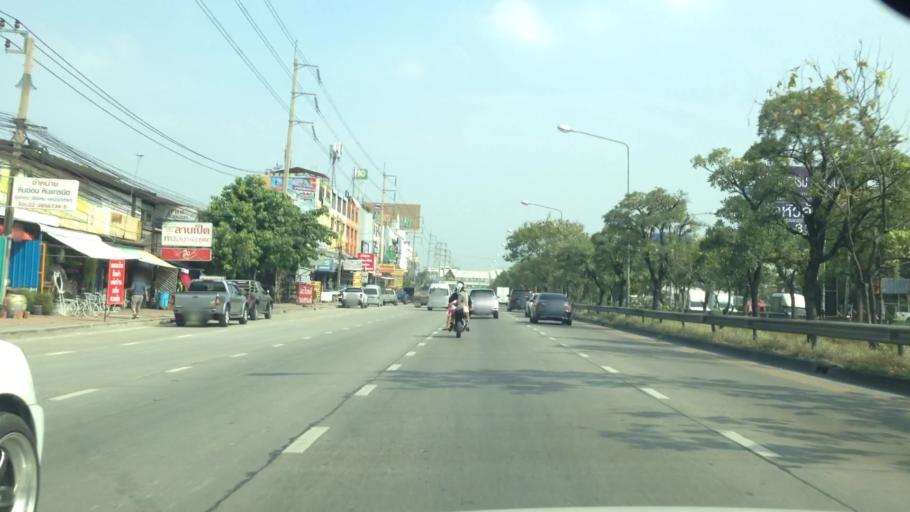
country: TH
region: Samut Prakan
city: Samut Prakan
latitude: 13.6168
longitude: 100.6213
